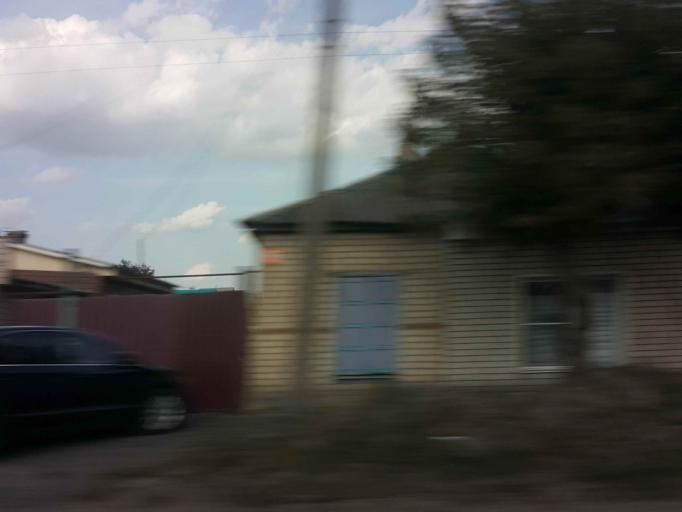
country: RU
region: Tambov
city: Tambov
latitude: 52.7149
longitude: 41.4395
